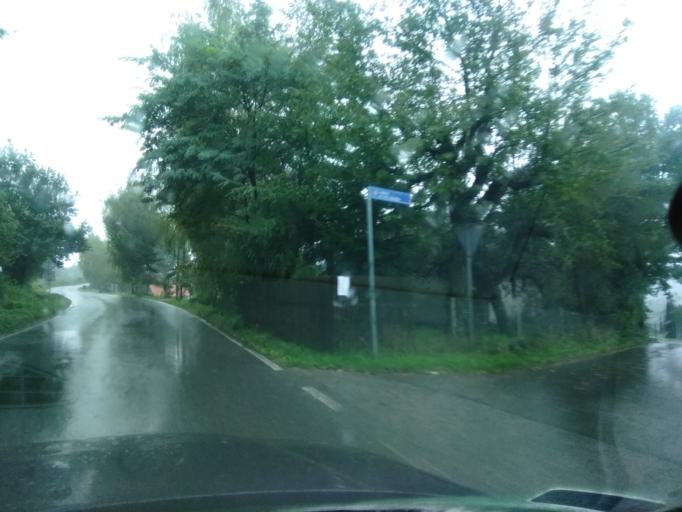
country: PL
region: Subcarpathian Voivodeship
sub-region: Powiat ropczycko-sedziszowski
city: Niedzwiada
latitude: 50.0471
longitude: 21.5377
